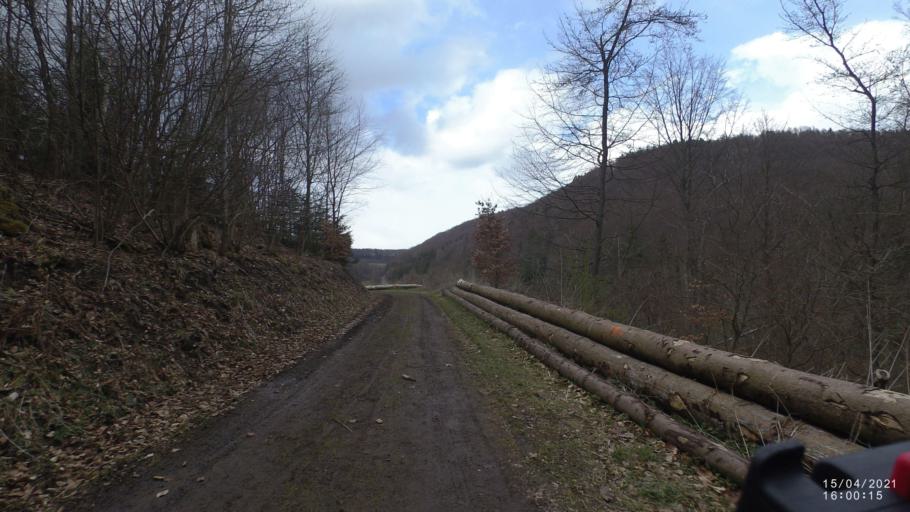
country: DE
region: Rheinland-Pfalz
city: Rieden
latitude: 50.3982
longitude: 7.1888
